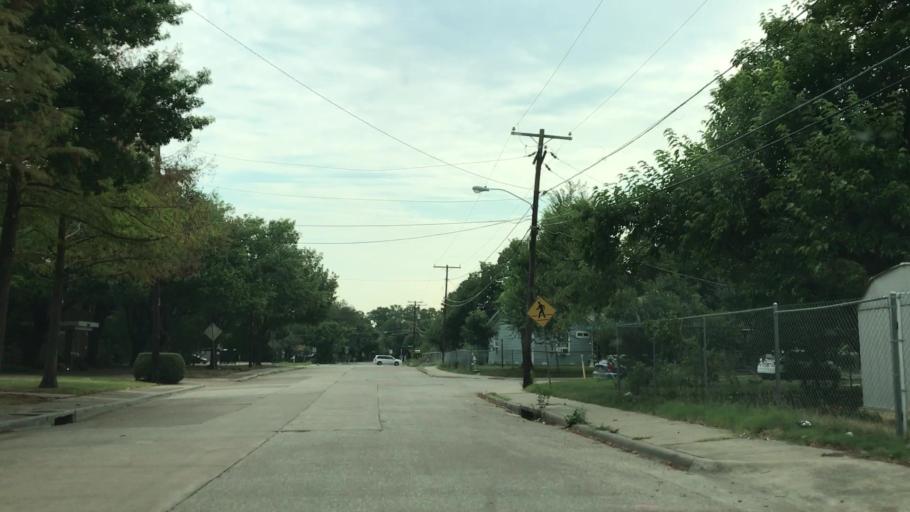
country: US
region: Texas
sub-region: Dallas County
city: Cockrell Hill
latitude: 32.7771
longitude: -96.9120
